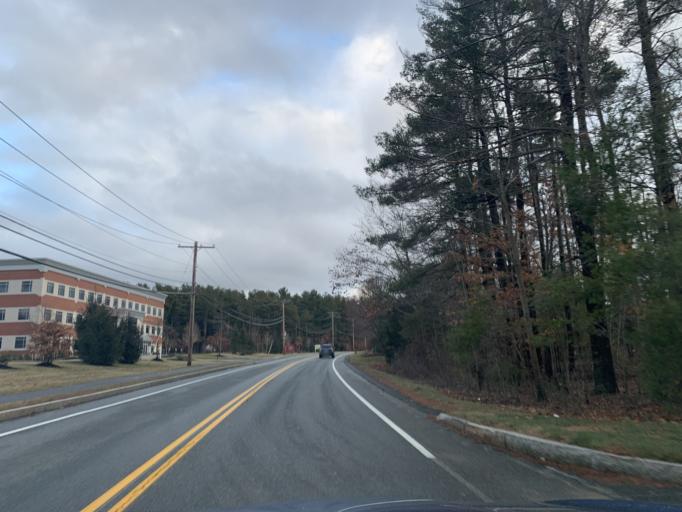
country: US
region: Massachusetts
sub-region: Norfolk County
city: Wrentham
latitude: 42.0902
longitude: -71.2968
